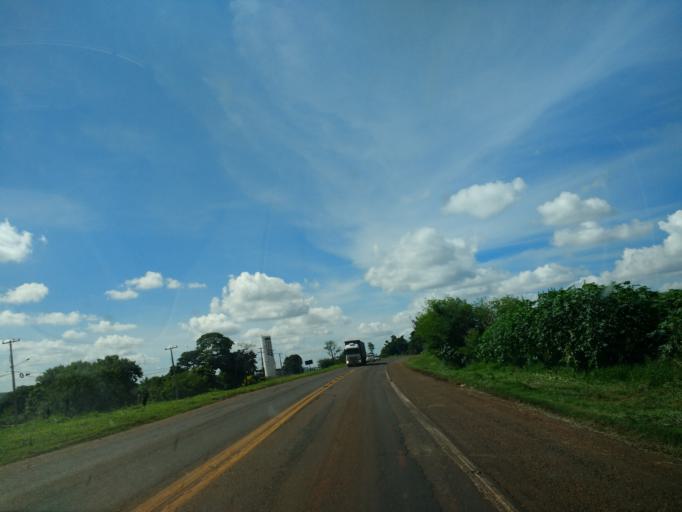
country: BR
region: Parana
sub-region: Paicandu
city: Paicandu
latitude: -23.4714
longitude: -52.0668
